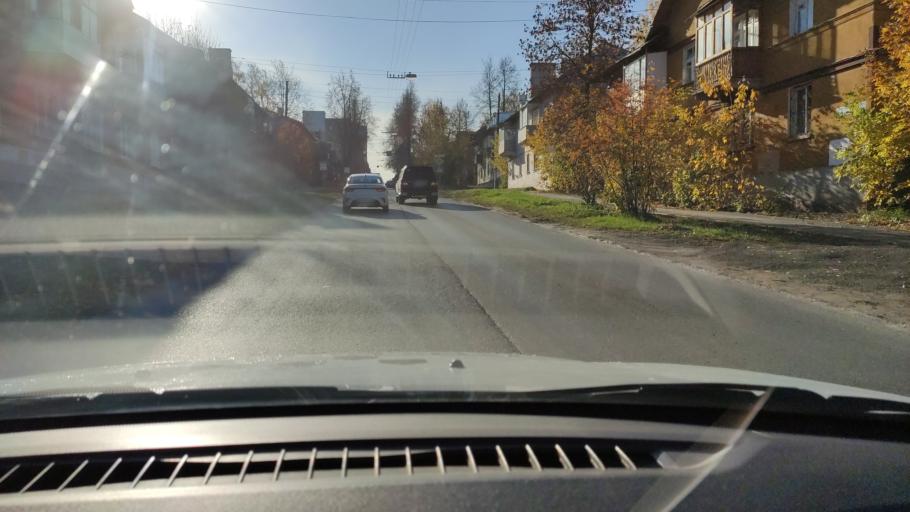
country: RU
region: Perm
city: Kondratovo
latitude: 57.9735
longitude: 56.1745
